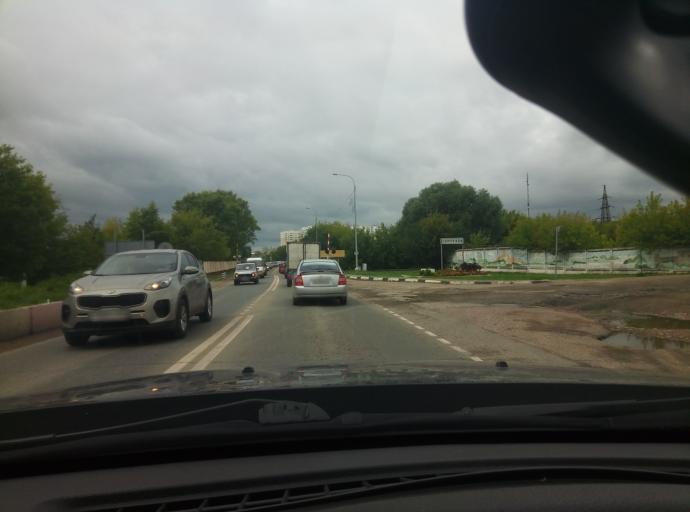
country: RU
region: Moskovskaya
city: Serpukhov
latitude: 54.9131
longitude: 37.4566
